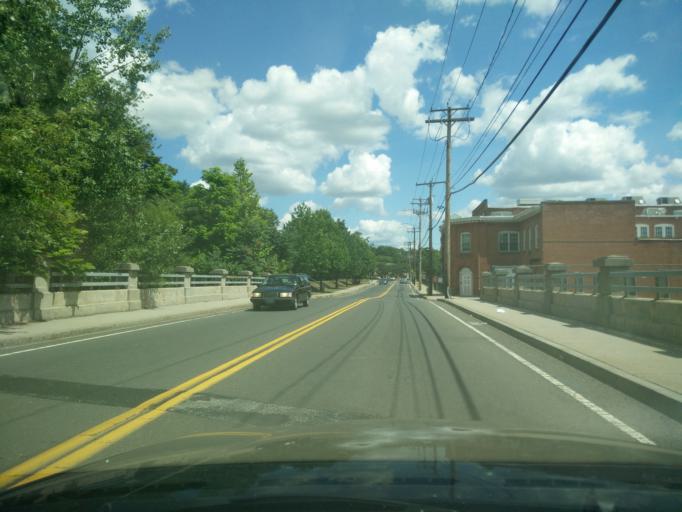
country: US
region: Connecticut
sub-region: New Haven County
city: New Haven
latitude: 41.3280
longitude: -72.9590
